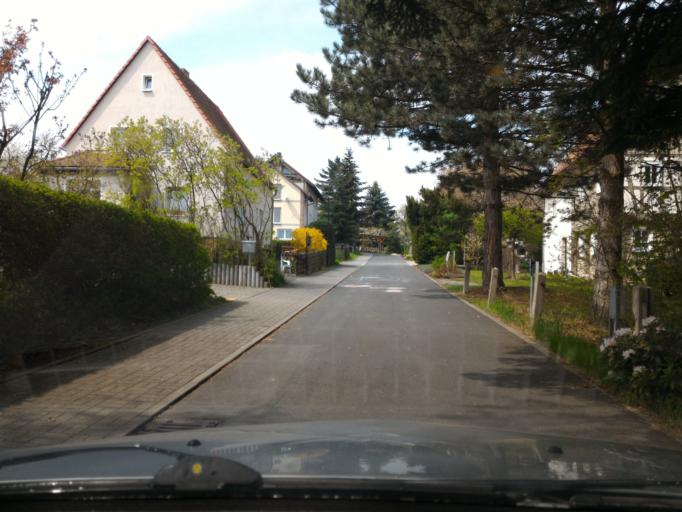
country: DE
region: Saxony
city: Bertsdorf-Hoernitz
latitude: 50.9040
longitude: 14.7365
